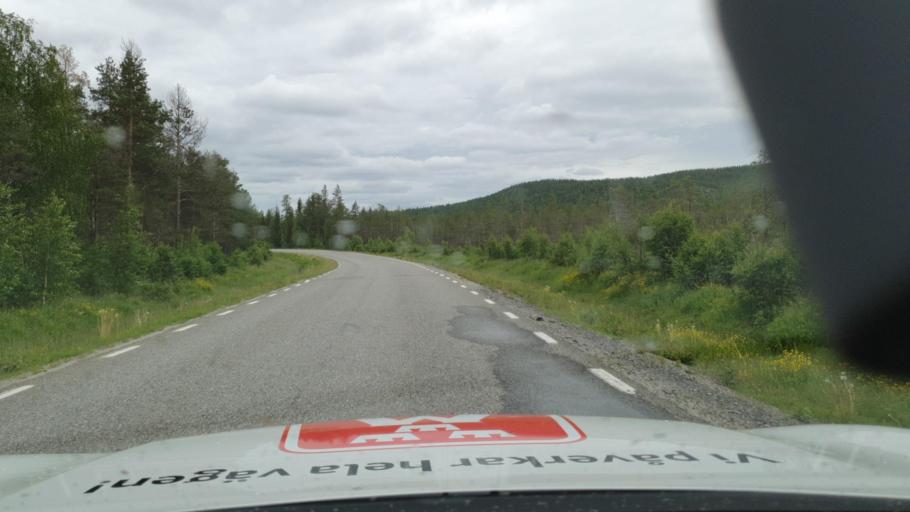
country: SE
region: Vaesterbotten
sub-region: Lycksele Kommun
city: Soderfors
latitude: 64.2680
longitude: 18.2032
